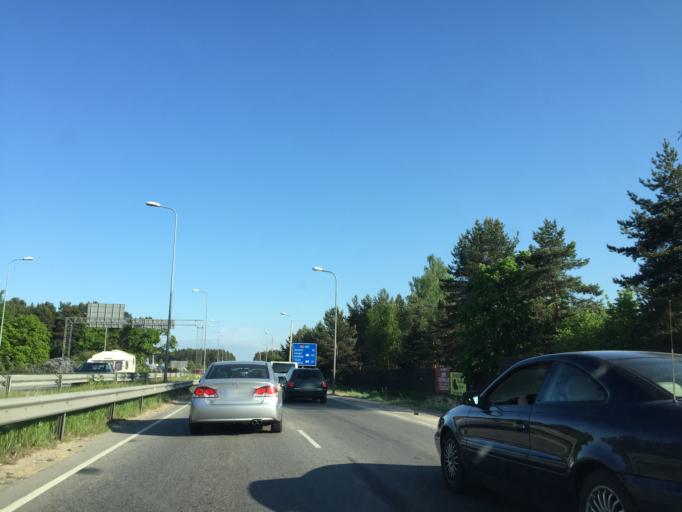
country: LV
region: Kekava
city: Balozi
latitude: 56.8990
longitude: 24.1362
